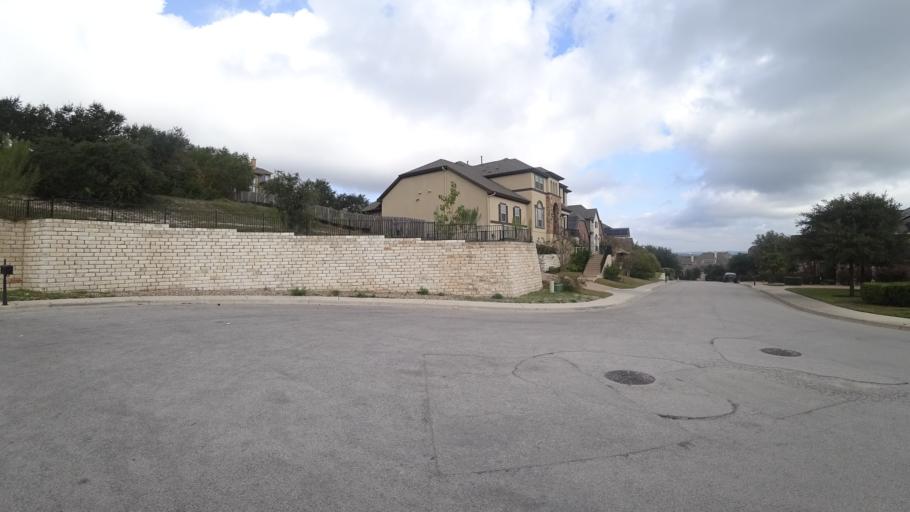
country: US
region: Texas
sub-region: Travis County
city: Barton Creek
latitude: 30.3137
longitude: -97.8980
